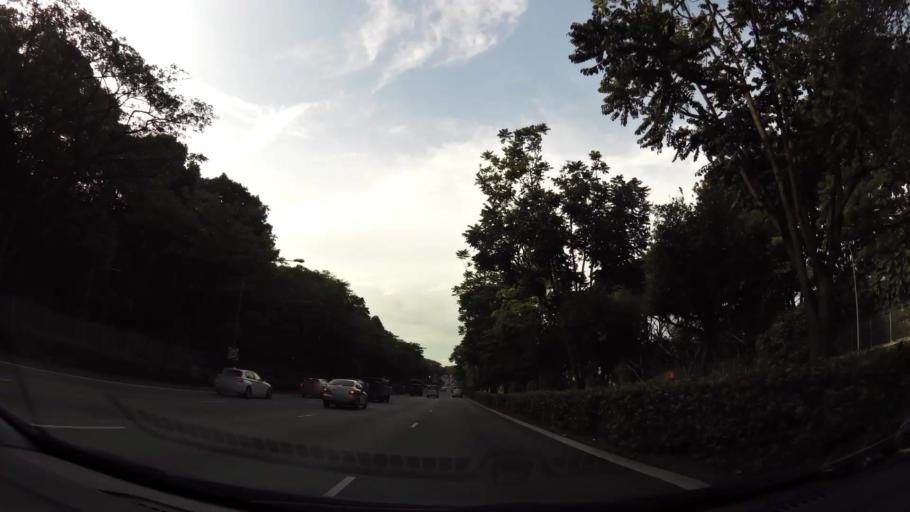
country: MY
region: Johor
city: Johor Bahru
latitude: 1.3362
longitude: 103.6768
